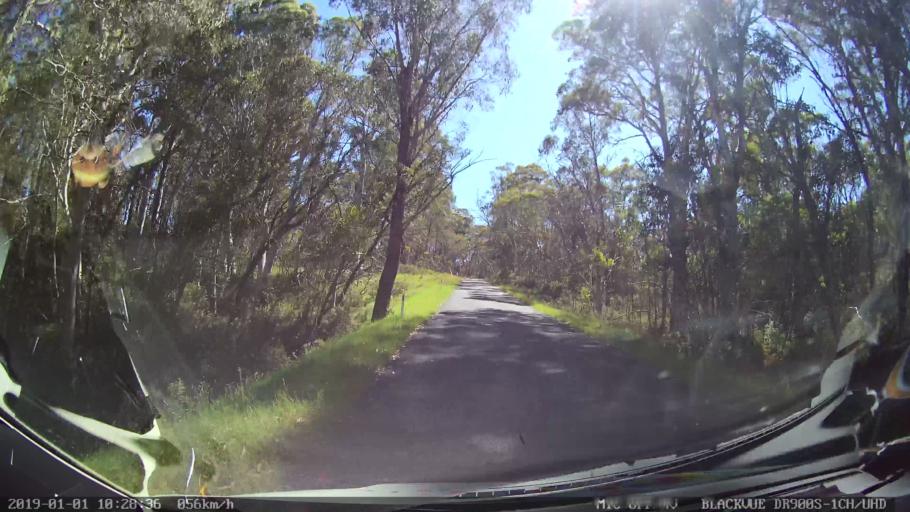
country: AU
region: New South Wales
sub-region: Snowy River
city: Jindabyne
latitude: -36.0593
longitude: 148.2419
